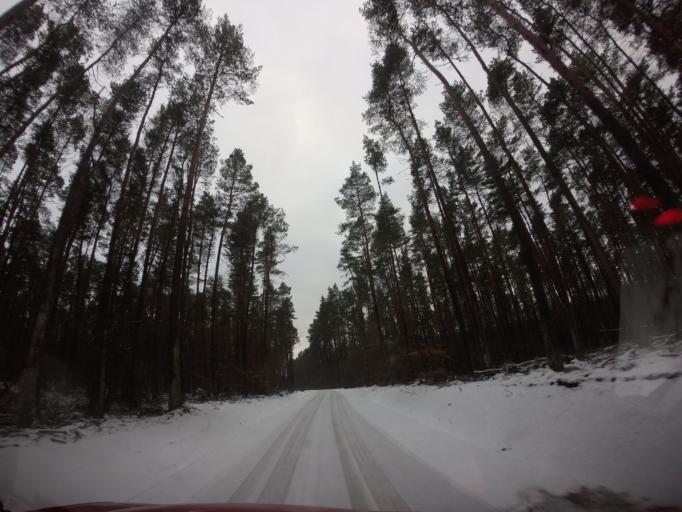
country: PL
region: West Pomeranian Voivodeship
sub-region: Powiat choszczenski
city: Pelczyce
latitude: 52.9526
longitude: 15.3505
